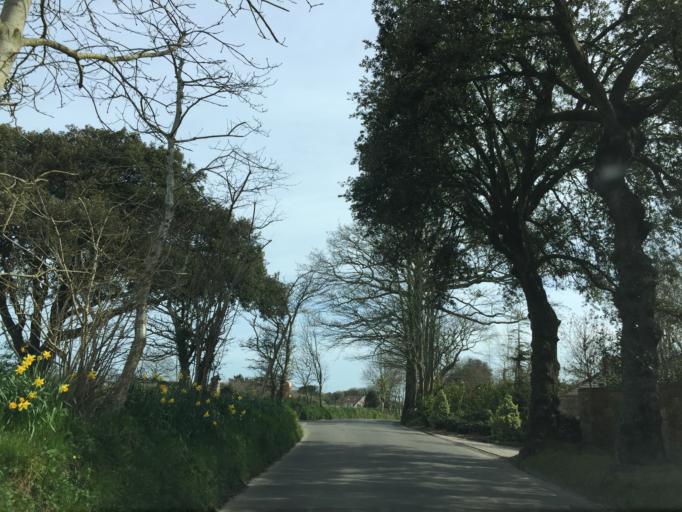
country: JE
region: St Helier
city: Saint Helier
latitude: 49.2284
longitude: -2.1135
